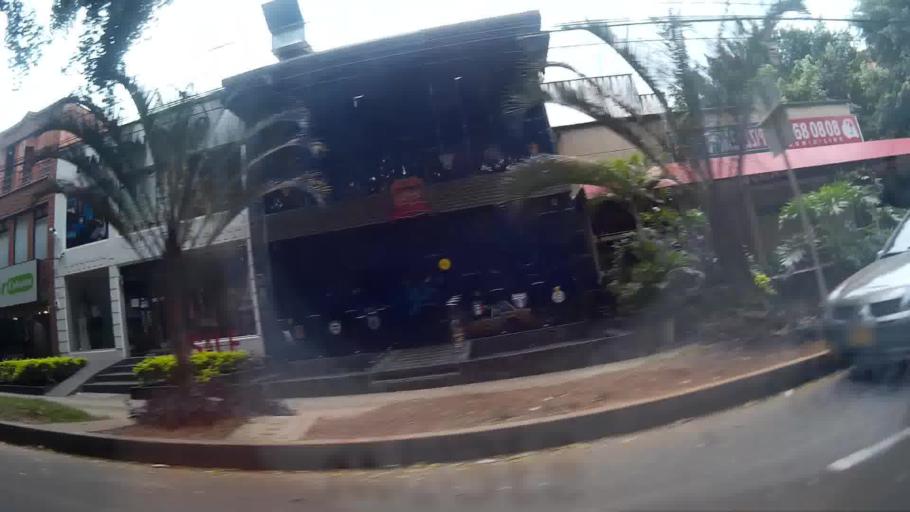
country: CO
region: Antioquia
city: Medellin
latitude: 6.2451
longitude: -75.5952
